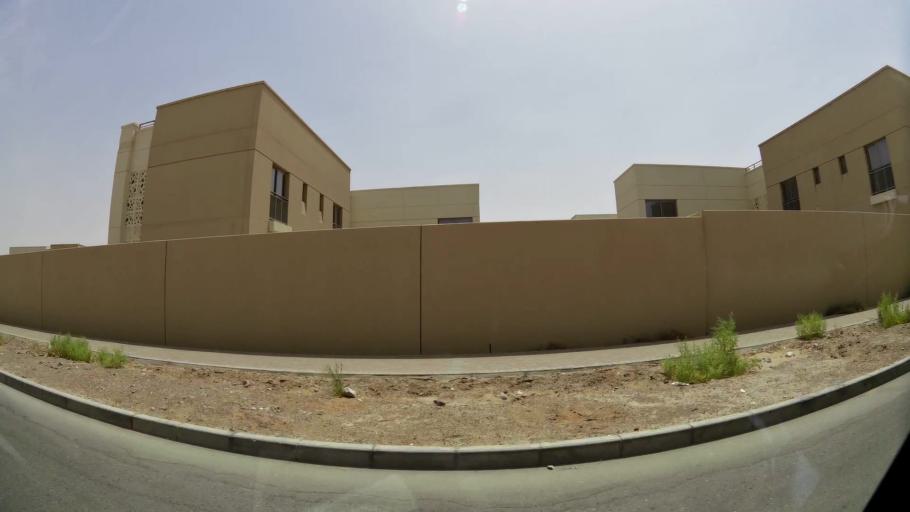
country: AE
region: Abu Dhabi
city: Al Ain
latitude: 24.1458
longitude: 55.6271
